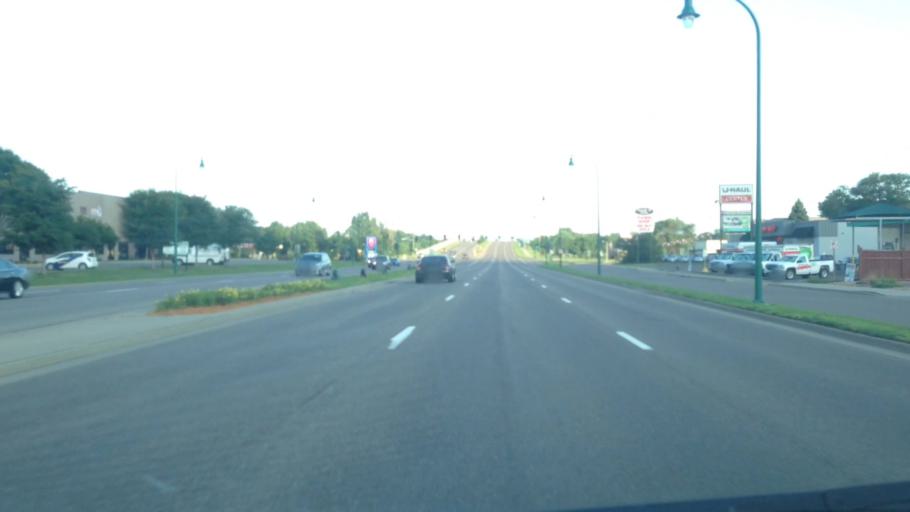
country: US
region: Minnesota
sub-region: Hennepin County
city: Crystal
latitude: 45.0531
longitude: -93.3569
